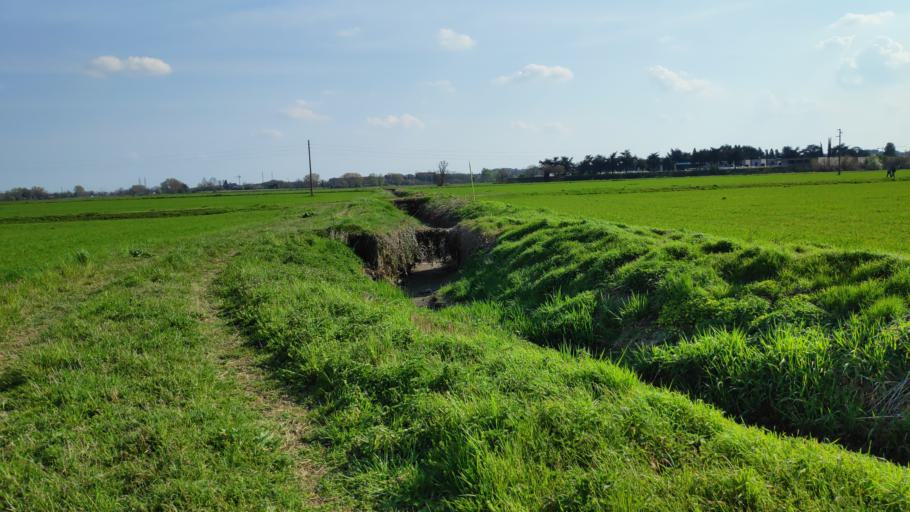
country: IT
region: Lombardy
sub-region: Citta metropolitana di Milano
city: San Giuliano Milanese
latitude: 45.4140
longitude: 9.2907
